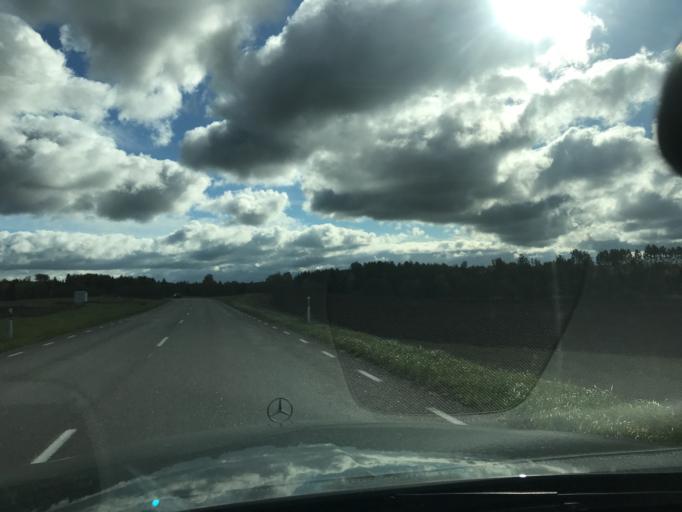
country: EE
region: Vorumaa
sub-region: Antsla vald
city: Vana-Antsla
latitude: 57.9069
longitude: 26.4224
